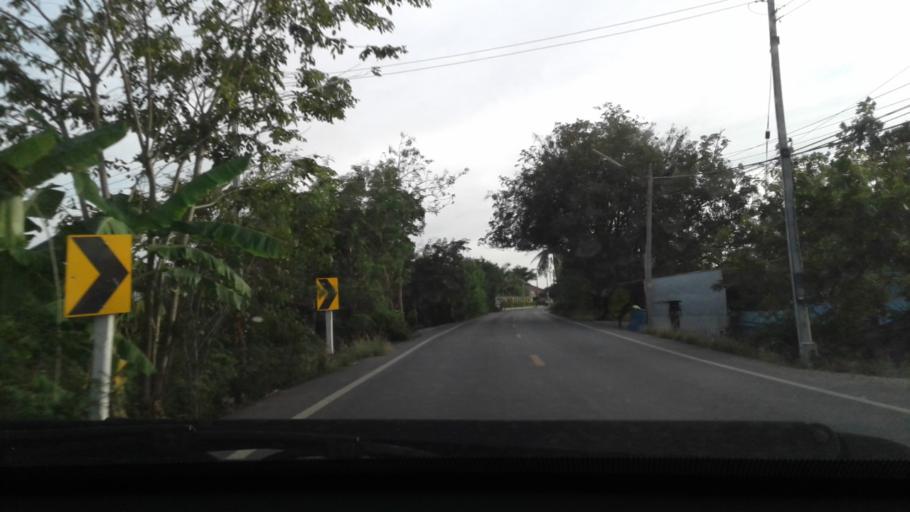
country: TH
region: Nonthaburi
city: Sai Noi
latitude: 13.9073
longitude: 100.2575
